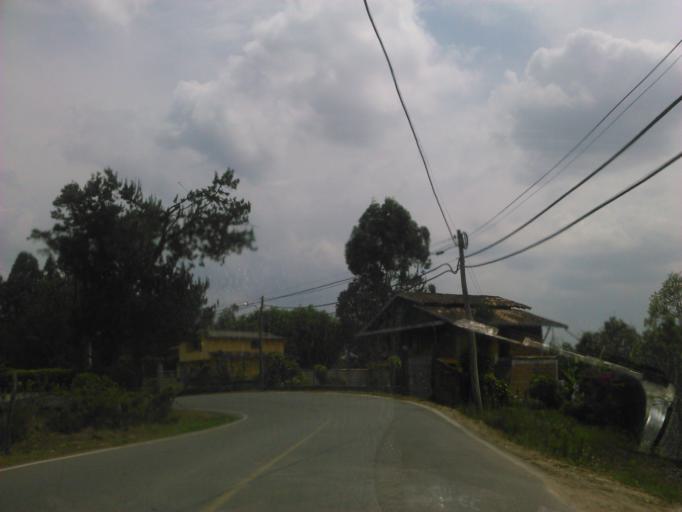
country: CO
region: Antioquia
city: San Vicente
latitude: 6.2314
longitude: -75.3862
